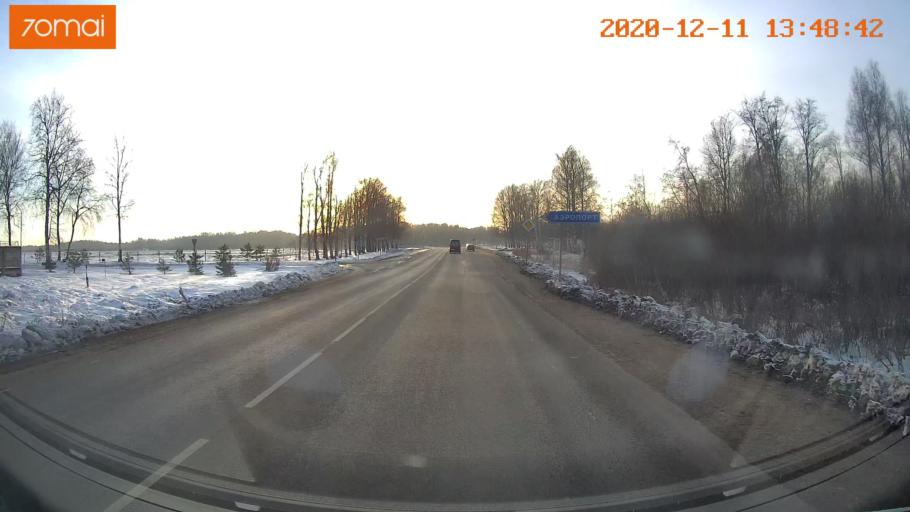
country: RU
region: Kostroma
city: Oktyabr'skiy
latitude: 57.8090
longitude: 41.0107
